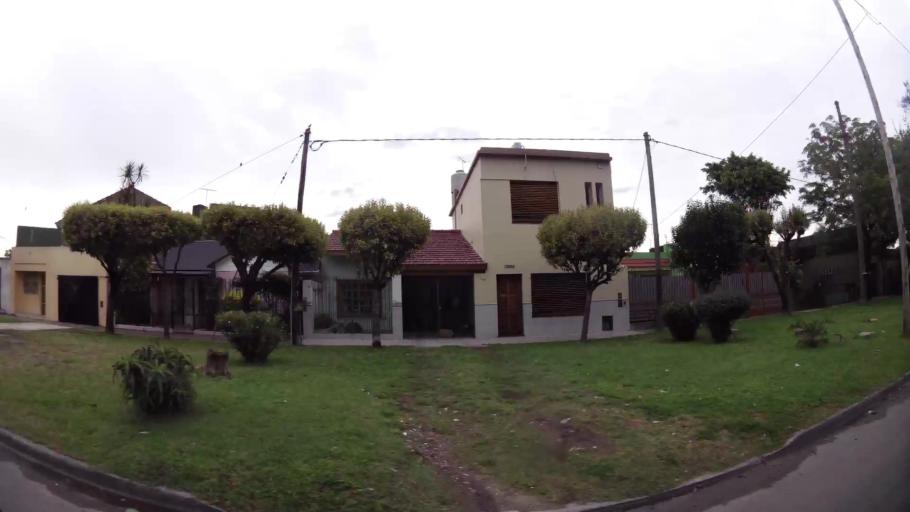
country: AR
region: Buenos Aires
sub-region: Partido de Lanus
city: Lanus
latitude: -34.7160
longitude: -58.3512
